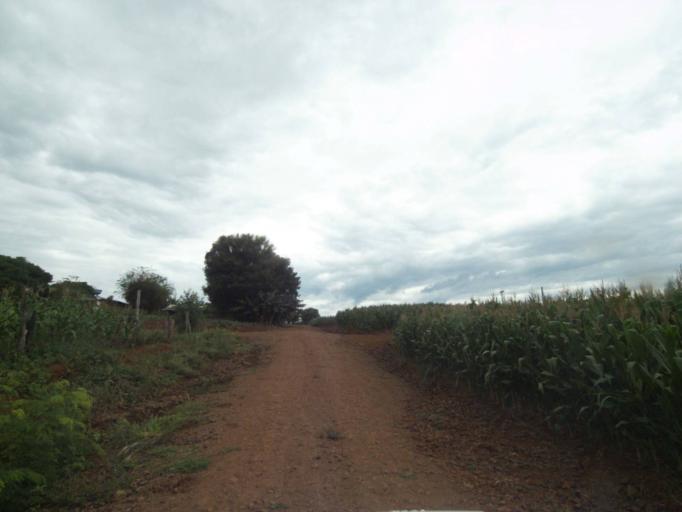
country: BR
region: Parana
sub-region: Guaraniacu
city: Guaraniacu
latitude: -24.9218
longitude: -52.9406
